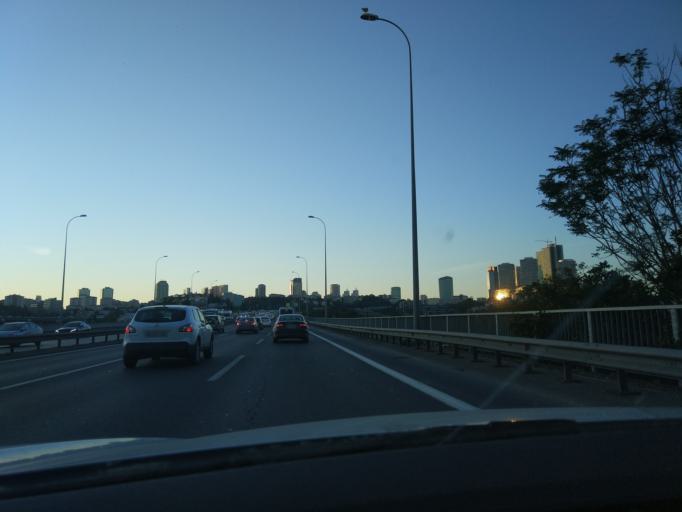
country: TR
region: Istanbul
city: UEskuedar
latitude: 41.0545
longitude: 29.0245
